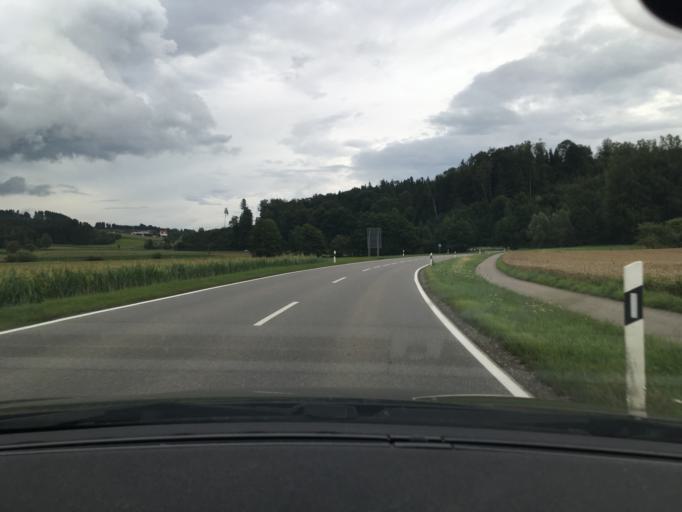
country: DE
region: Baden-Wuerttemberg
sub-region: Tuebingen Region
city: Markdorf
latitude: 47.7737
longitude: 9.4059
